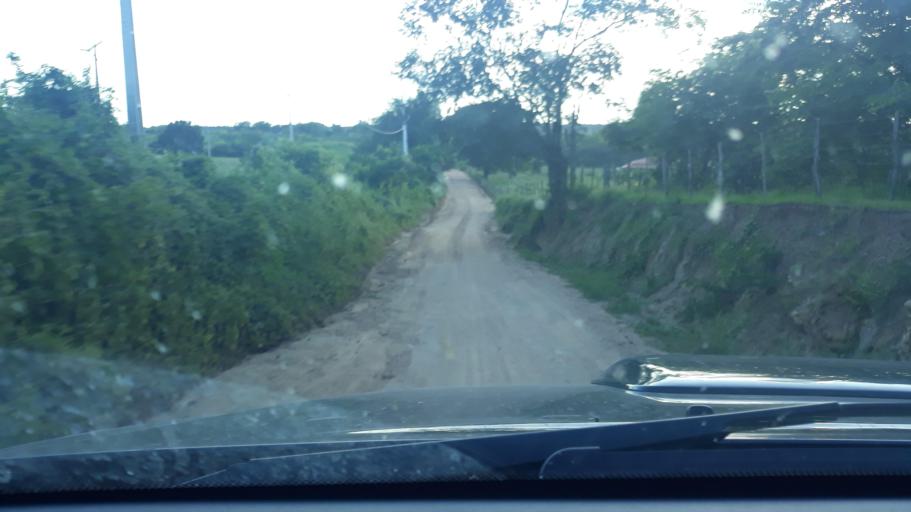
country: BR
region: Bahia
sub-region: Riacho De Santana
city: Riacho de Santana
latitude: -13.8057
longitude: -42.7138
